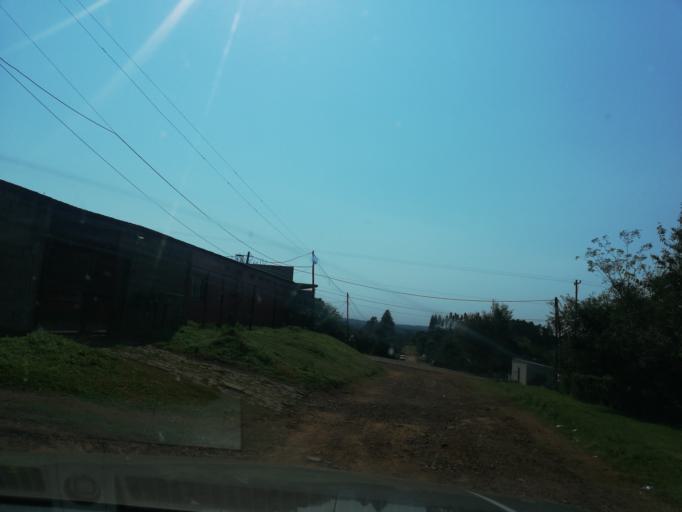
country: AR
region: Misiones
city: Bonpland
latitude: -27.4810
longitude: -55.4803
